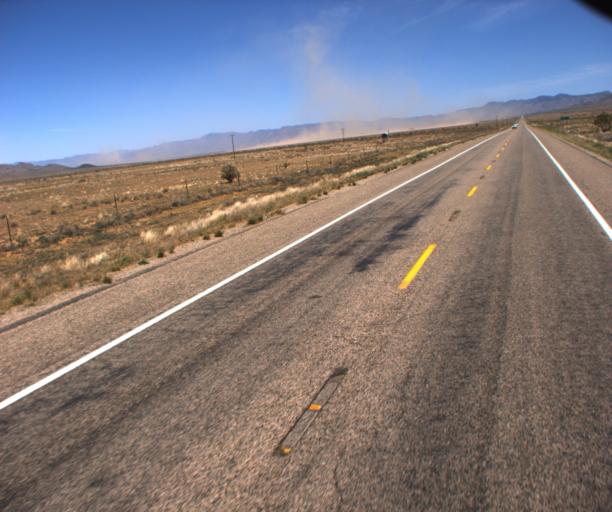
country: US
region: Arizona
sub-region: Mohave County
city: New Kingman-Butler
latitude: 35.3225
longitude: -113.9100
